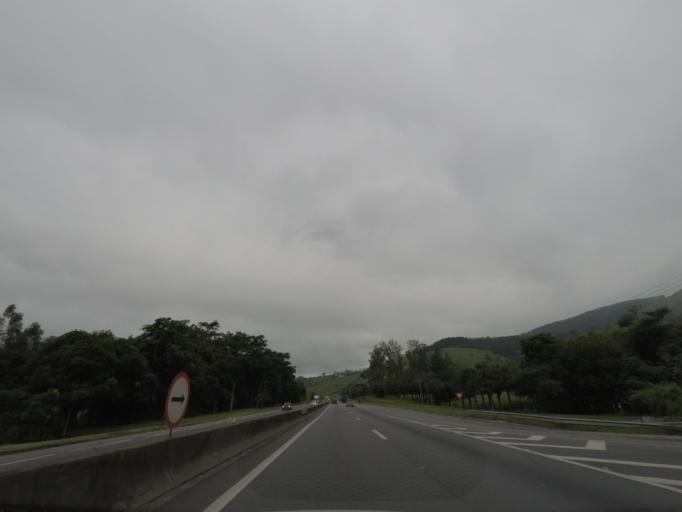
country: BR
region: Sao Paulo
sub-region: Aparecida
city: Aparecida
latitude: -22.8734
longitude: -45.2530
